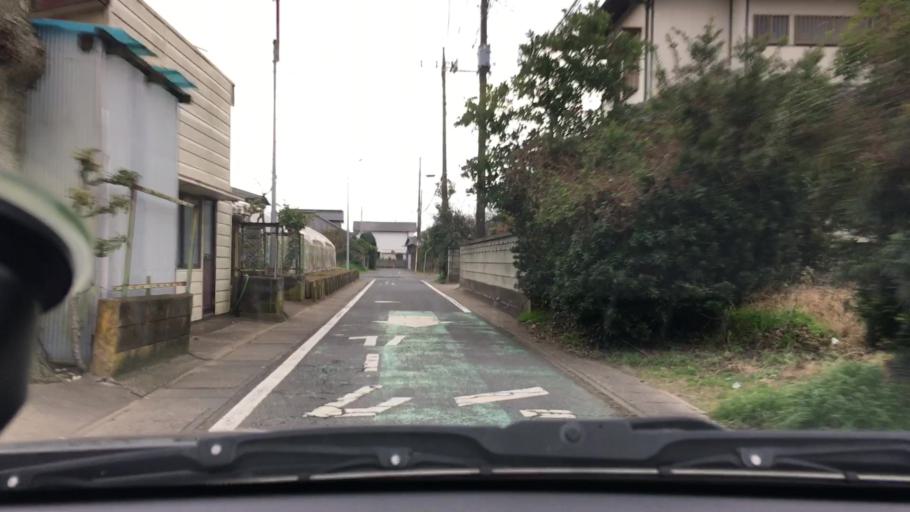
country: JP
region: Chiba
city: Omigawa
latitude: 35.8677
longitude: 140.6664
